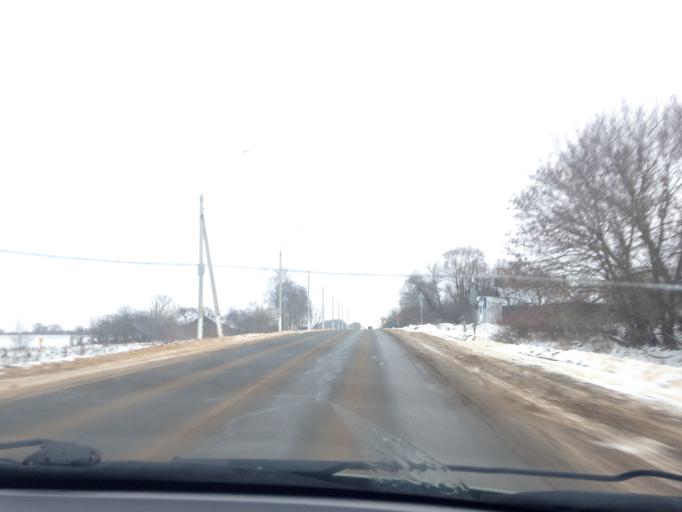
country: RU
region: Tula
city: Shchekino
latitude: 53.9549
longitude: 37.4916
